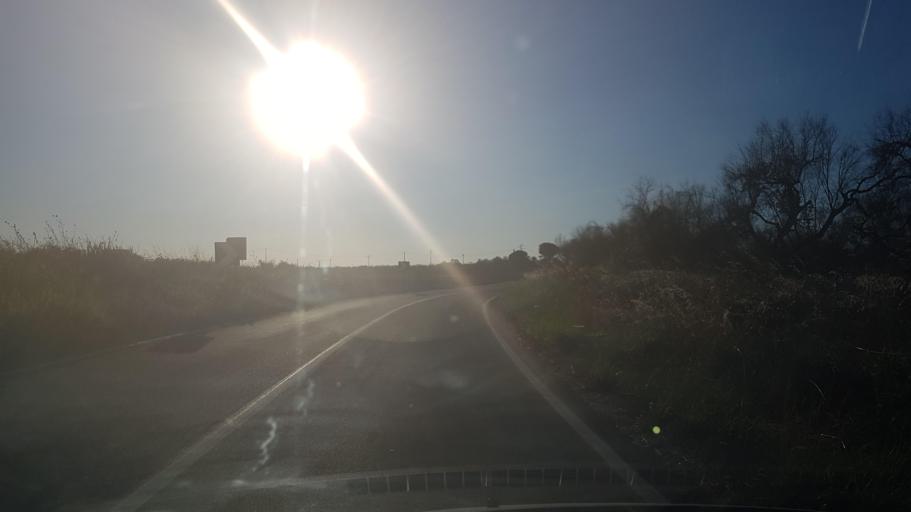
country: IT
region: Apulia
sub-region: Provincia di Lecce
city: Struda
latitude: 40.3295
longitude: 18.3025
